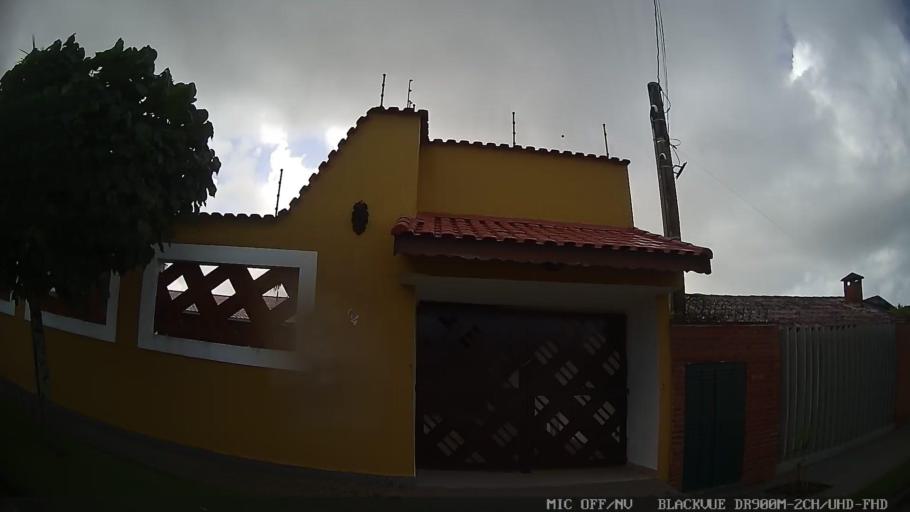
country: BR
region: Sao Paulo
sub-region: Itanhaem
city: Itanhaem
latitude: -24.1599
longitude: -46.7317
